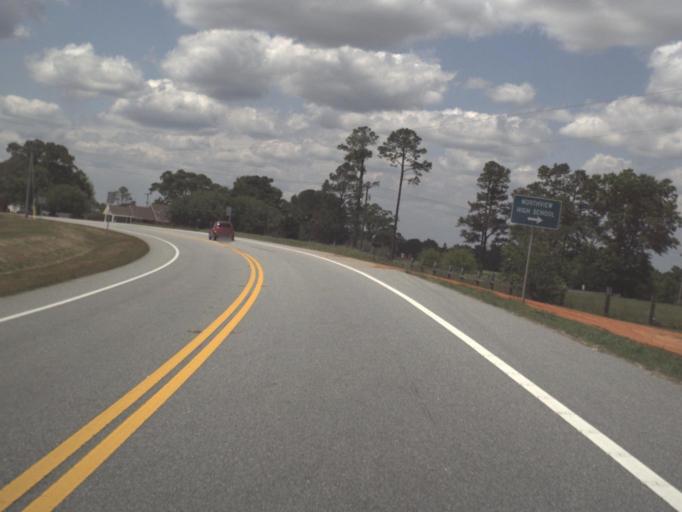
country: US
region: Alabama
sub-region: Escambia County
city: Atmore
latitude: 30.8847
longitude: -87.4503
